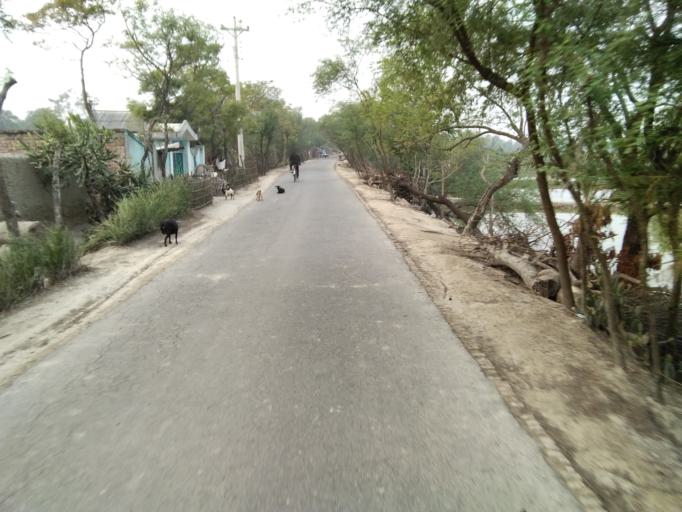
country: BD
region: Khulna
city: Satkhira
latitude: 22.5812
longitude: 89.0682
